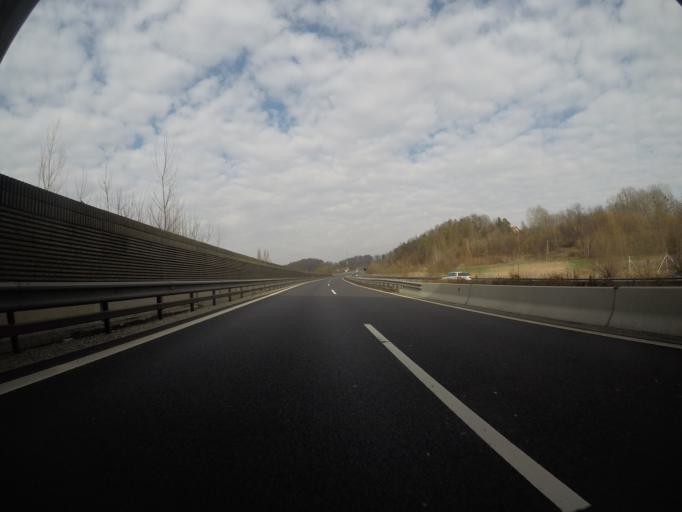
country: SI
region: Cerkvenjak
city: Cerkvenjak
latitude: 46.5711
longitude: 15.9304
